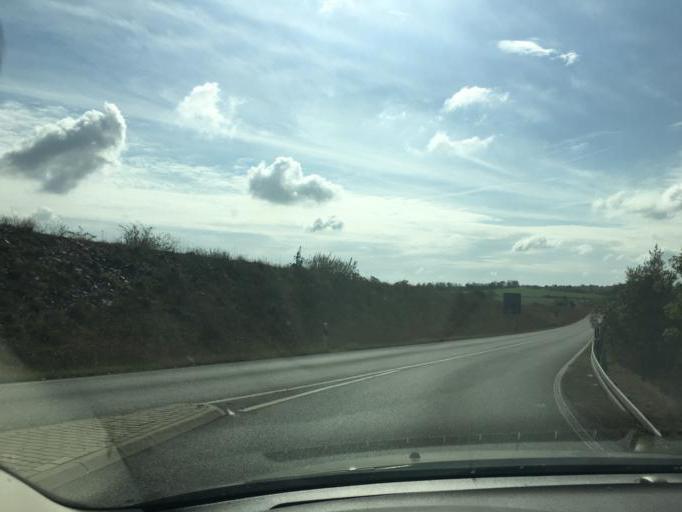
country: DE
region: Thuringia
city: Geroda
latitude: 50.7550
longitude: 11.9040
